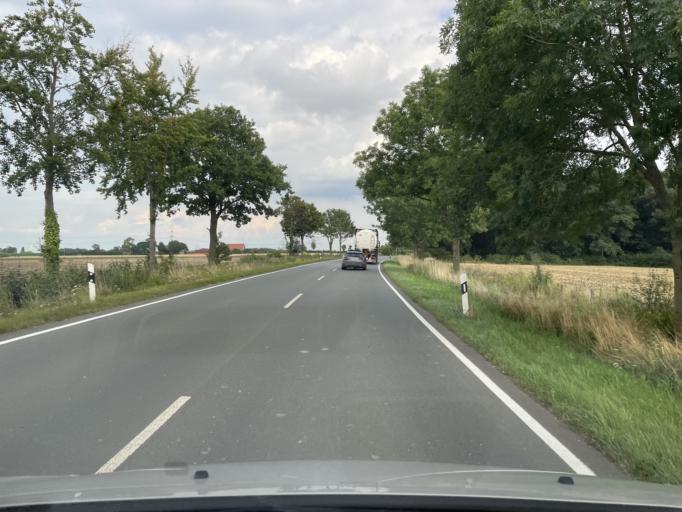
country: DE
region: North Rhine-Westphalia
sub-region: Regierungsbezirk Arnsberg
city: Hamm
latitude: 51.7511
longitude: 7.8134
